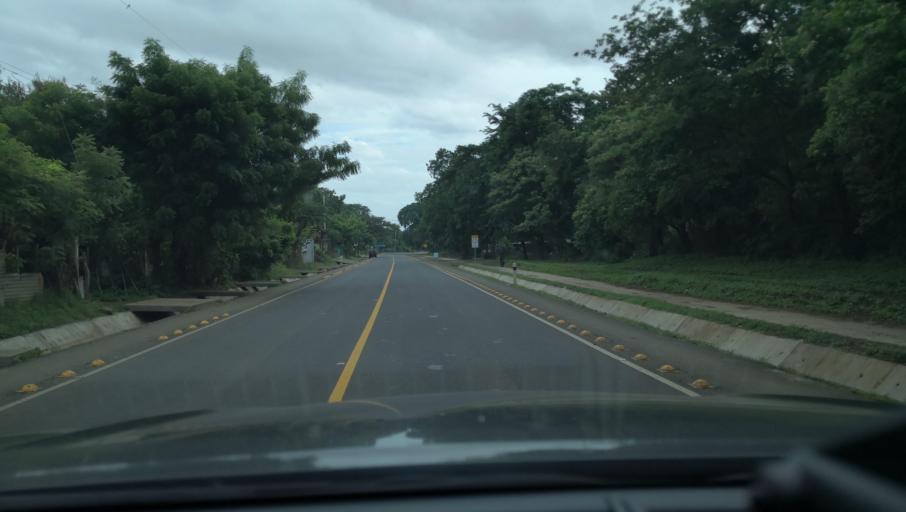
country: NI
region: Masaya
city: Nindiri
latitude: 12.0668
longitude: -86.1379
